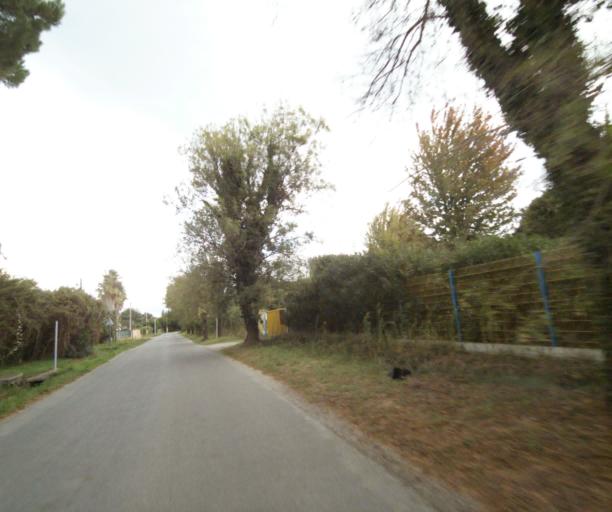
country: FR
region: Languedoc-Roussillon
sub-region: Departement des Pyrenees-Orientales
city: Argelers
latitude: 42.5683
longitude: 3.0342
